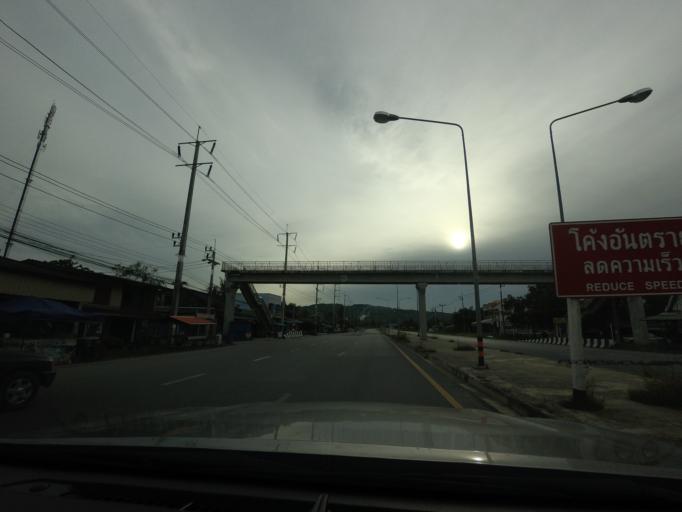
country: TH
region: Nakhon Si Thammarat
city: Hua Sai
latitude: 8.0513
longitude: 100.2163
